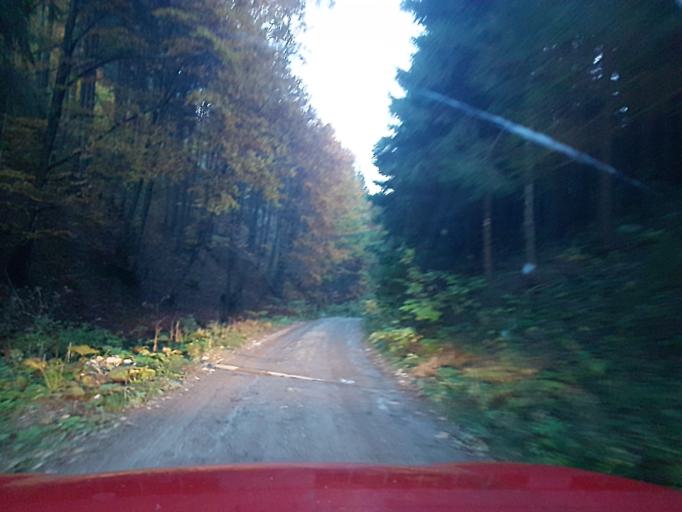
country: SK
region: Zilinsky
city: Ruzomberok
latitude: 49.1368
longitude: 19.3728
